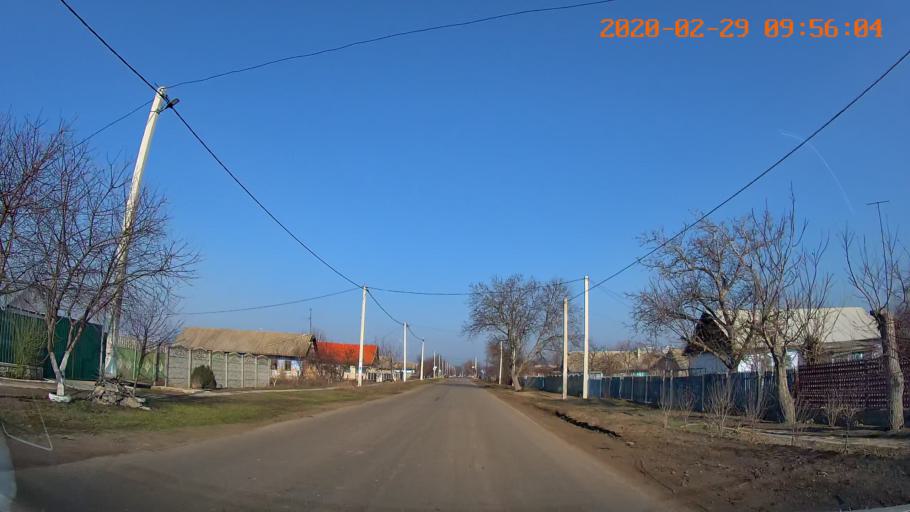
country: MD
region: Telenesti
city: Slobozia
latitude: 46.7393
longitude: 29.7068
